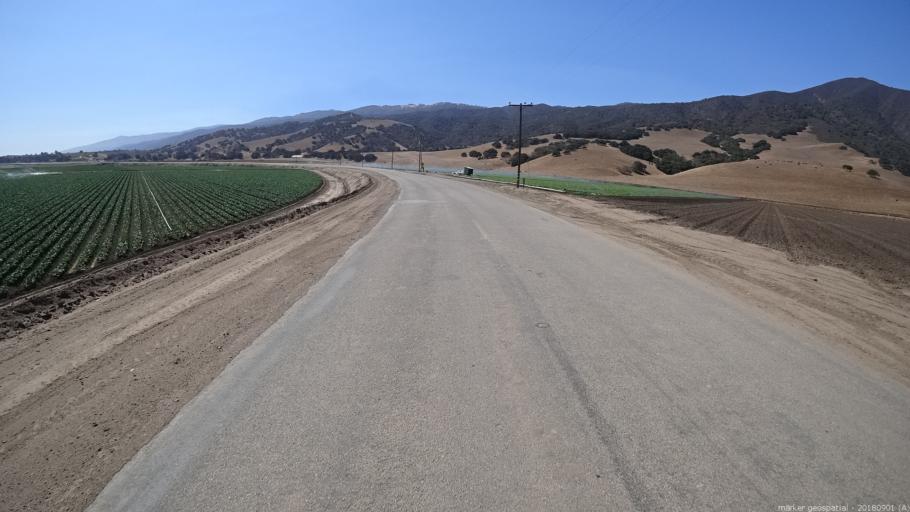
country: US
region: California
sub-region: Monterey County
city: Chualar
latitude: 36.5378
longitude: -121.5416
